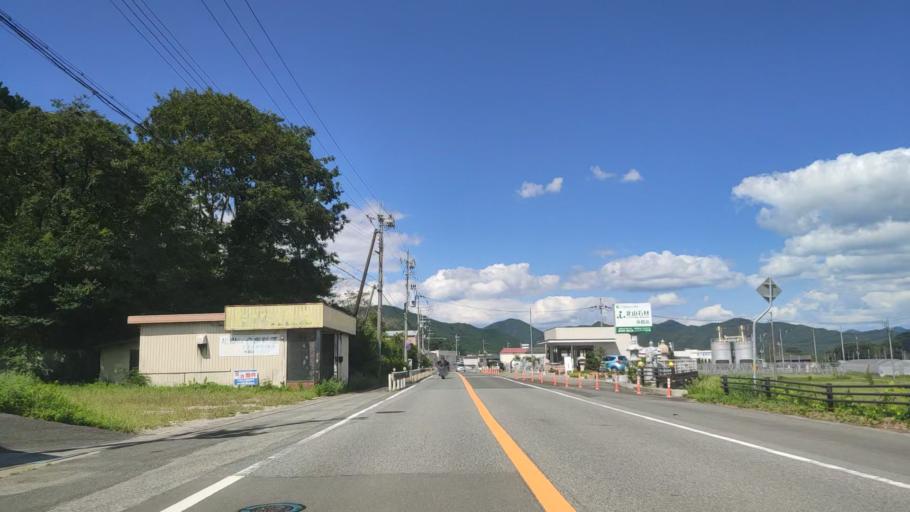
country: JP
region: Kyoto
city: Fukuchiyama
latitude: 35.2176
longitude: 135.1318
